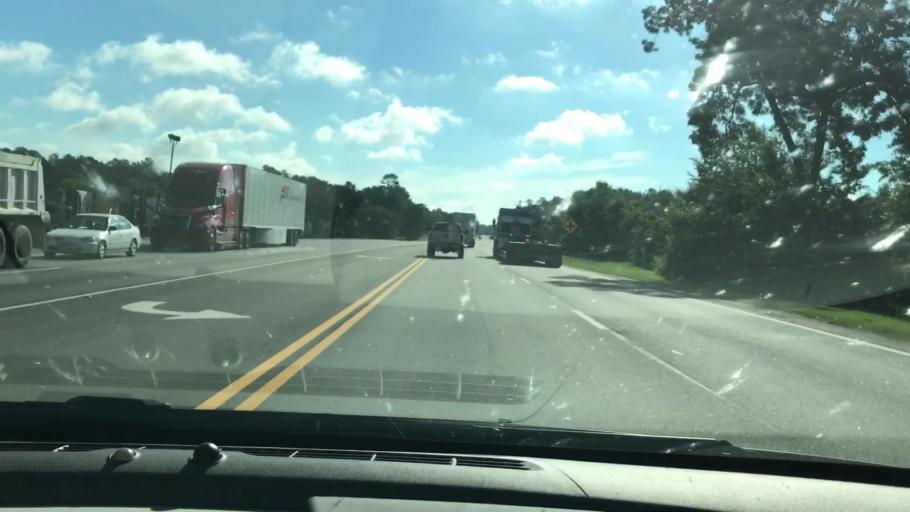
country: US
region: Georgia
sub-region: Dougherty County
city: Albany
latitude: 31.5800
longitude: -84.0870
